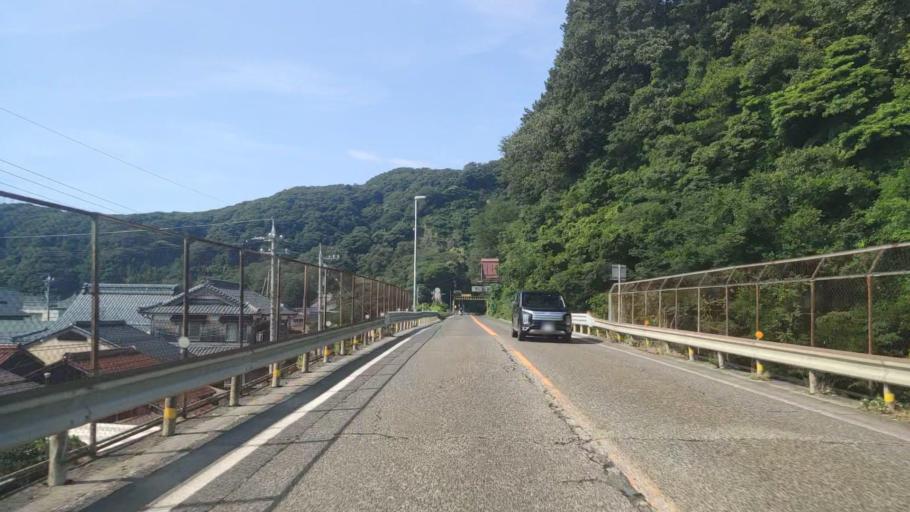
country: JP
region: Fukui
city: Tsuruga
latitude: 35.6597
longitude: 136.0772
